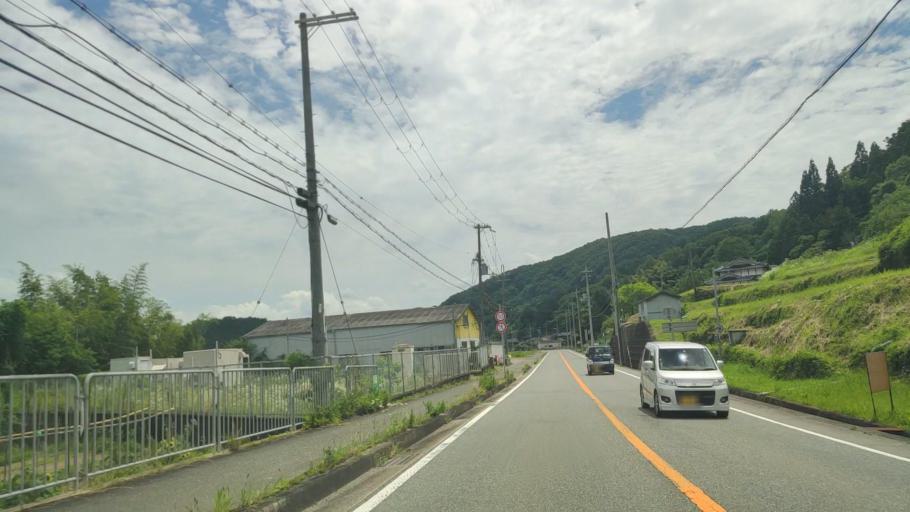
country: JP
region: Hyogo
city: Yamazakicho-nakabirose
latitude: 35.0400
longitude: 134.3691
